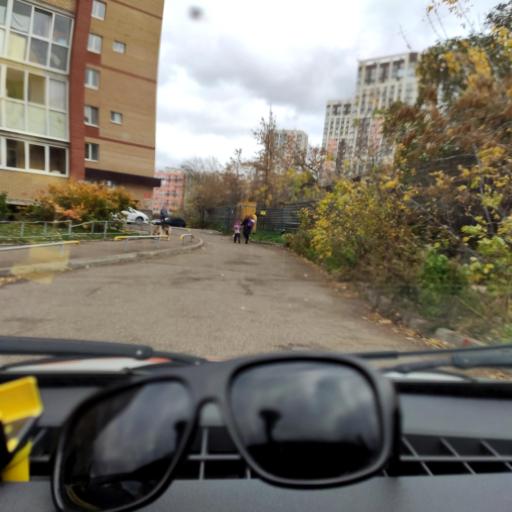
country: RU
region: Bashkortostan
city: Ufa
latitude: 54.7145
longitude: 55.9773
